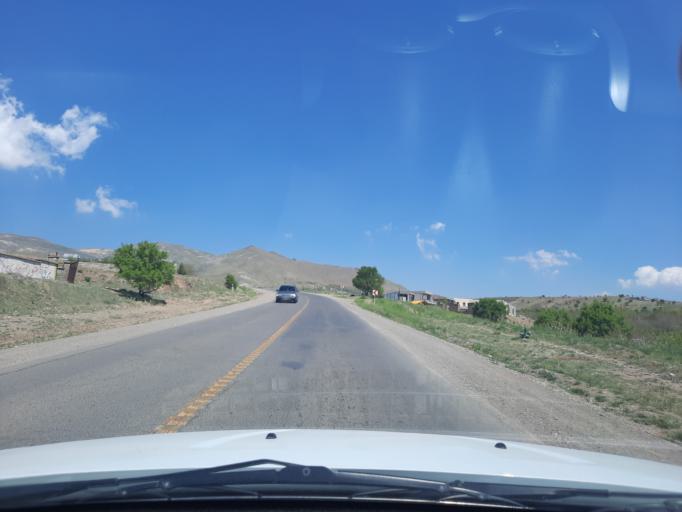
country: IR
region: Qazvin
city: Qazvin
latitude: 36.3462
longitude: 50.1822
